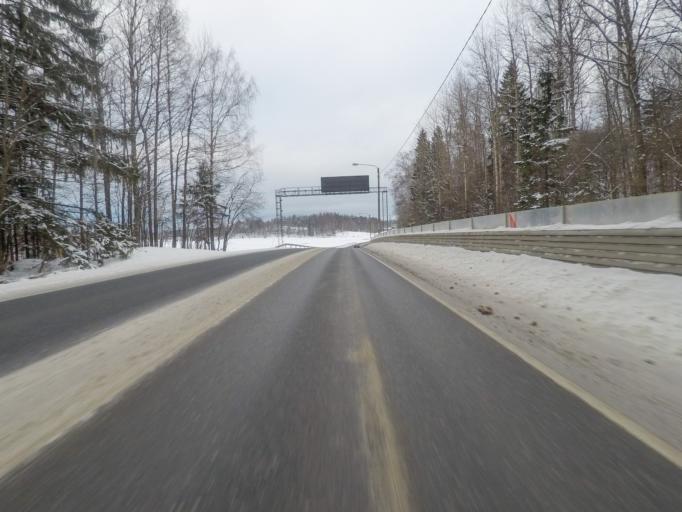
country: FI
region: Uusimaa
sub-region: Helsinki
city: Vantaa
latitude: 60.2388
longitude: 25.1374
